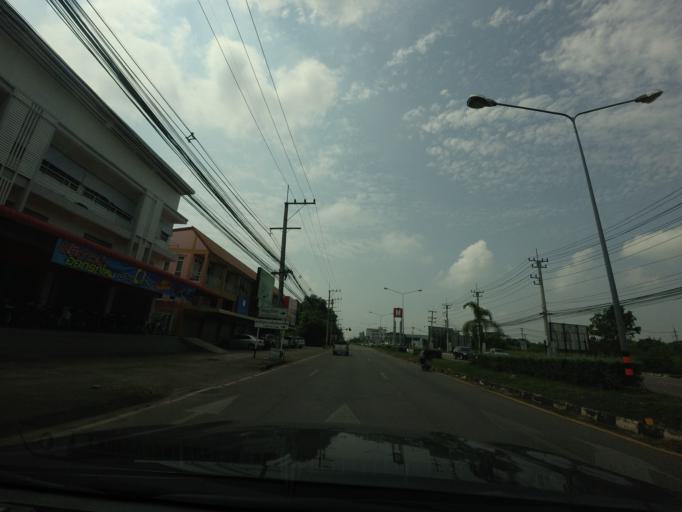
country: TH
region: Phrae
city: Phrae
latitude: 18.1265
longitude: 100.1427
